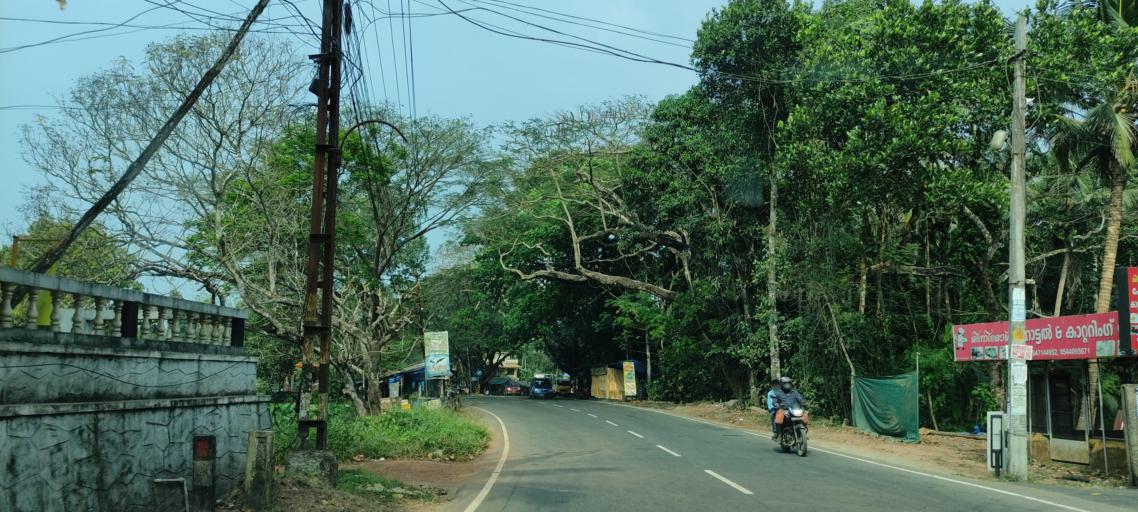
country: IN
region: Kerala
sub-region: Kottayam
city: Vaikam
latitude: 9.7691
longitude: 76.4181
